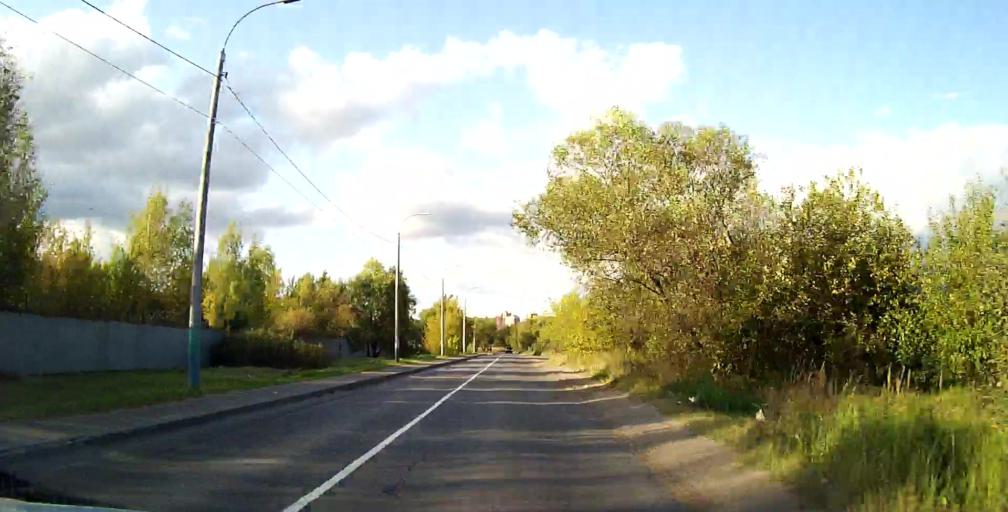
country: RU
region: Moskovskaya
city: Klimovsk
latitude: 55.3778
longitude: 37.5625
